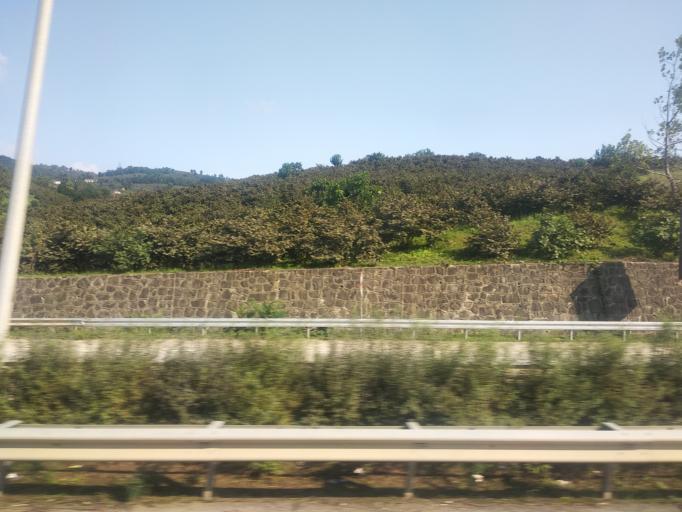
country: TR
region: Ordu
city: Ordu
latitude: 40.9943
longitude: 37.8174
